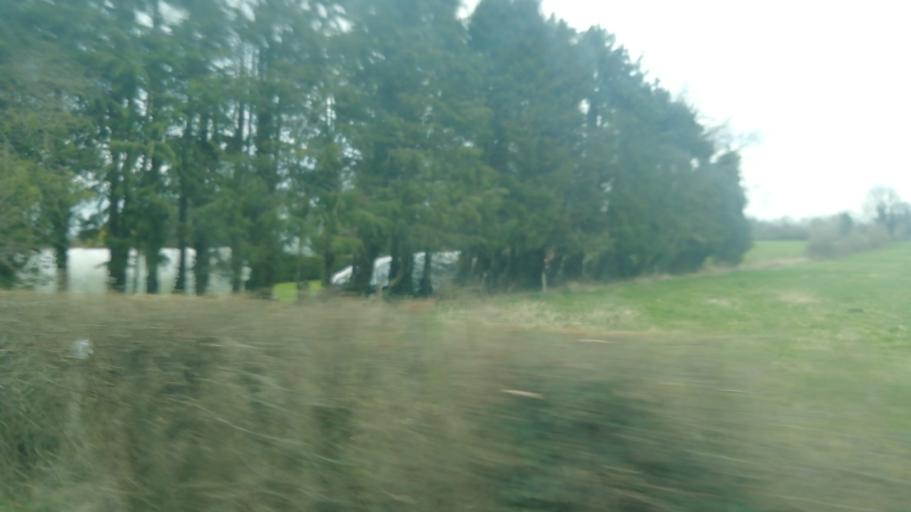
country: IE
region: Leinster
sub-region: Kildare
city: Derrinturn
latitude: 53.2826
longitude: -6.8955
